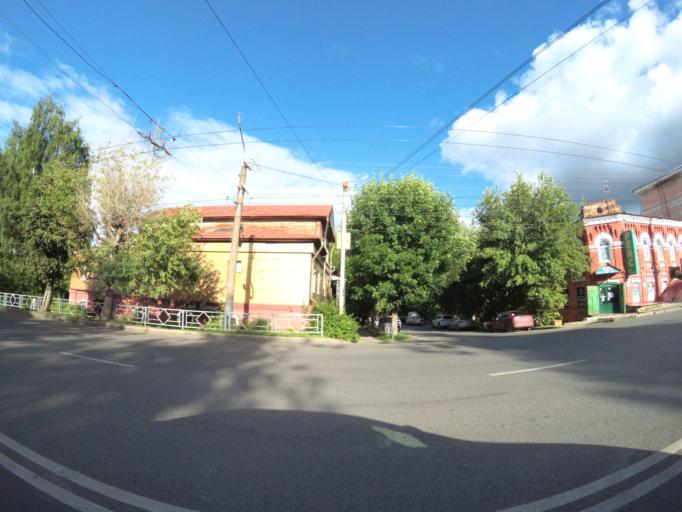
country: RU
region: Kirov
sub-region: Kirovo-Chepetskiy Rayon
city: Kirov
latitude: 58.6071
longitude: 49.6807
